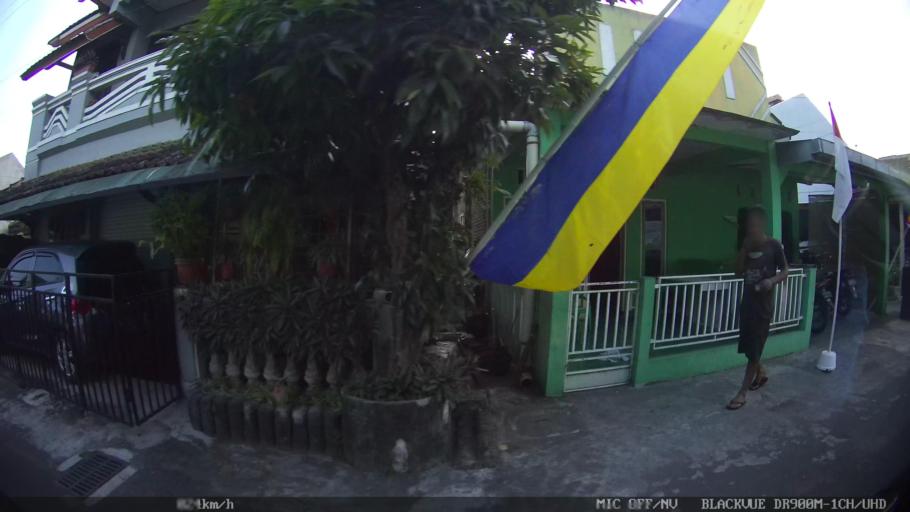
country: ID
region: Daerah Istimewa Yogyakarta
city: Yogyakarta
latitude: -7.7902
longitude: 110.3510
